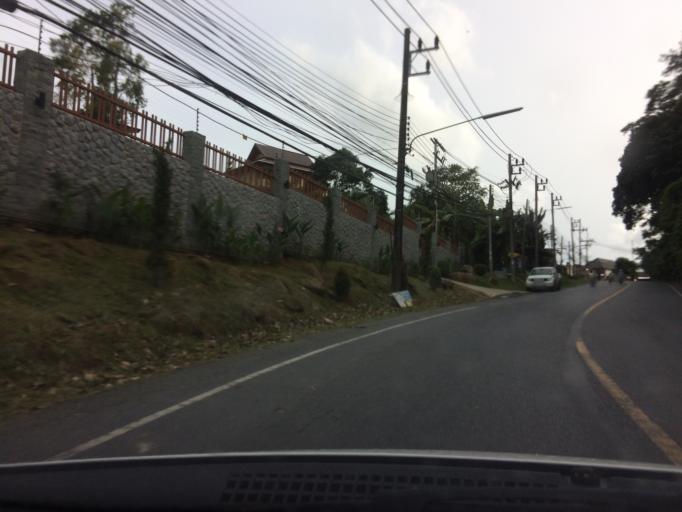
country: TH
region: Phuket
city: Phuket
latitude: 7.8961
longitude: 98.4096
